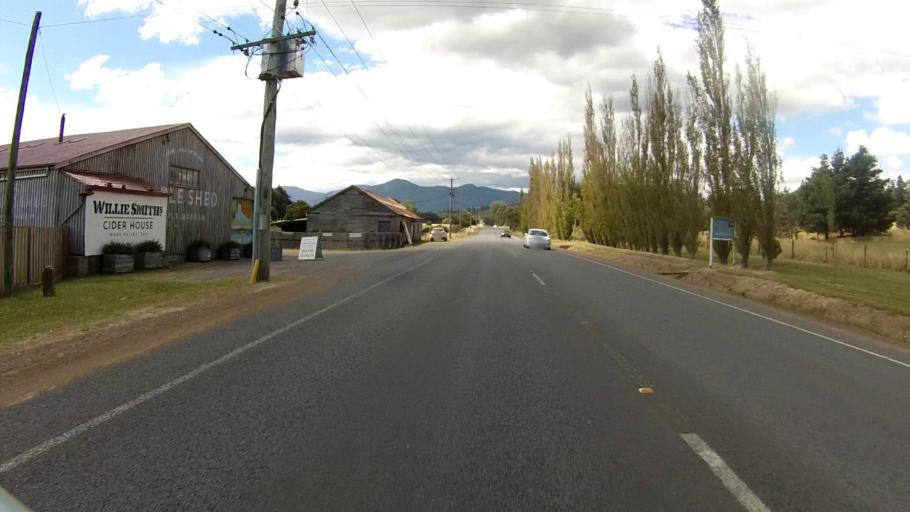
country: AU
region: Tasmania
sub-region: Huon Valley
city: Huonville
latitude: -42.9881
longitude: 147.0859
